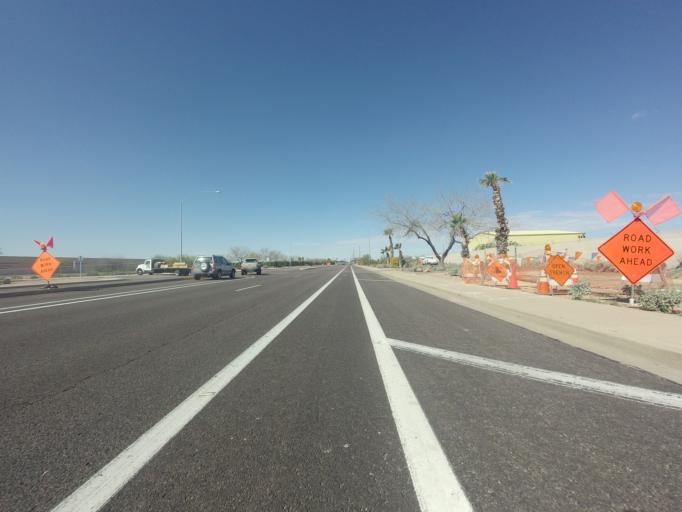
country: US
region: Arizona
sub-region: Maricopa County
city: Mesa
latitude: 33.4664
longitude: -111.7324
